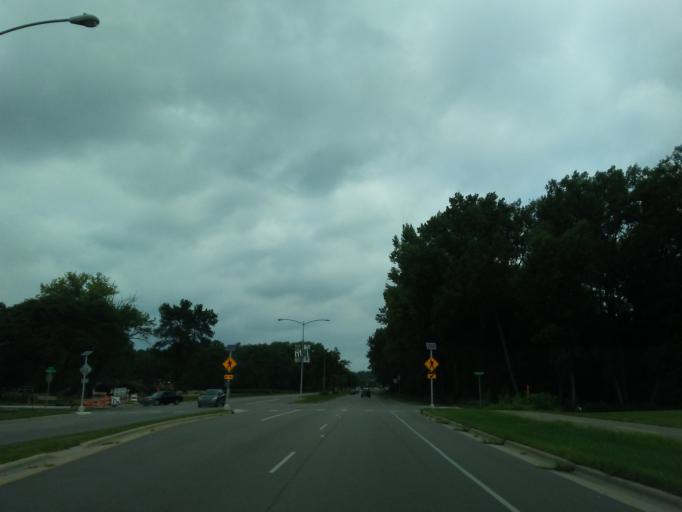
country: US
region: Wisconsin
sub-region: Dane County
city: Middleton
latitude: 43.0957
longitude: -89.4858
